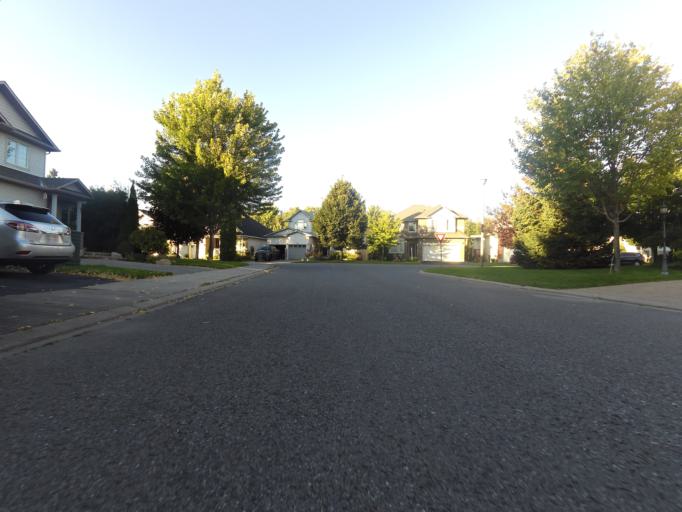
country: CA
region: Ontario
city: Ottawa
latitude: 45.2914
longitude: -75.7102
